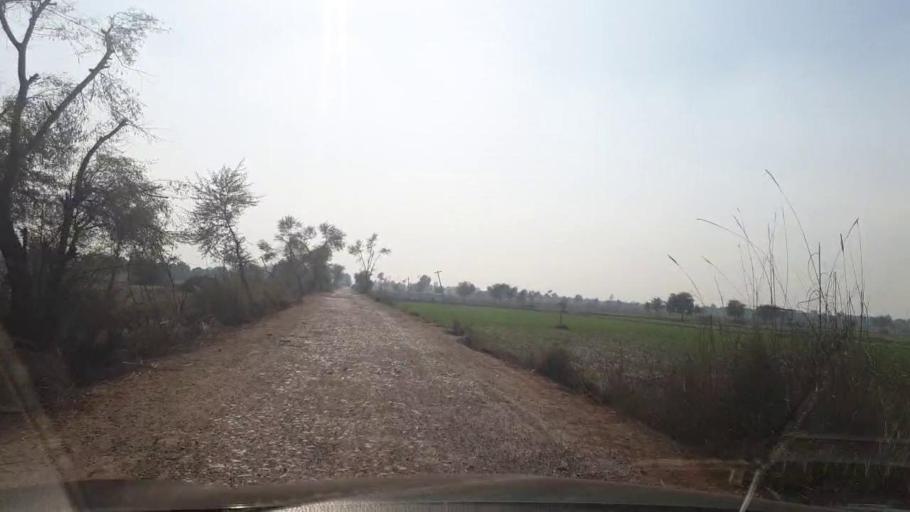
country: PK
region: Sindh
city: Khairpur
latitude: 28.1253
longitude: 69.6438
